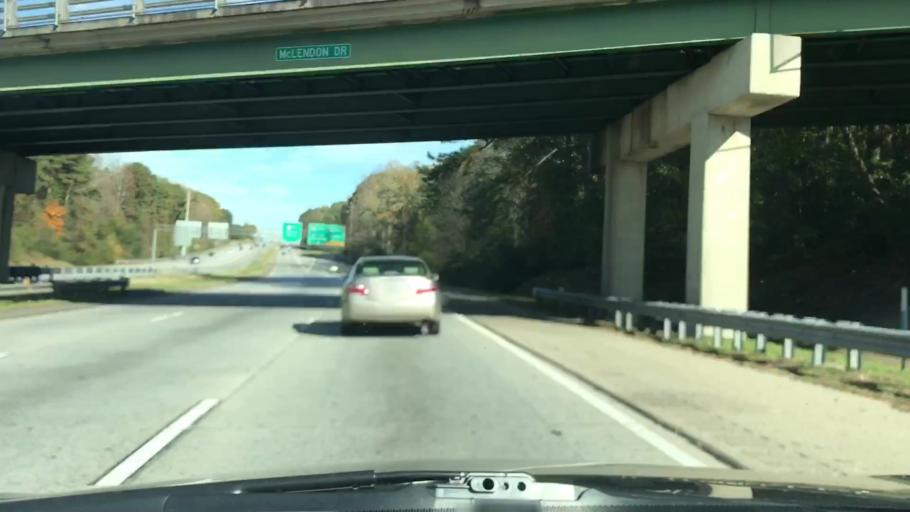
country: US
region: Georgia
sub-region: DeKalb County
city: Clarkston
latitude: 33.8112
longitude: -84.2608
